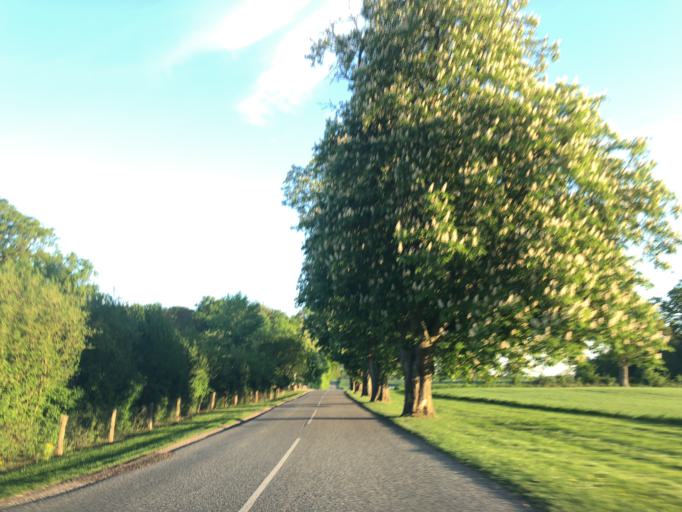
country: DK
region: Zealand
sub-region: Koge Kommune
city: Borup
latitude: 55.4183
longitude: 11.9310
